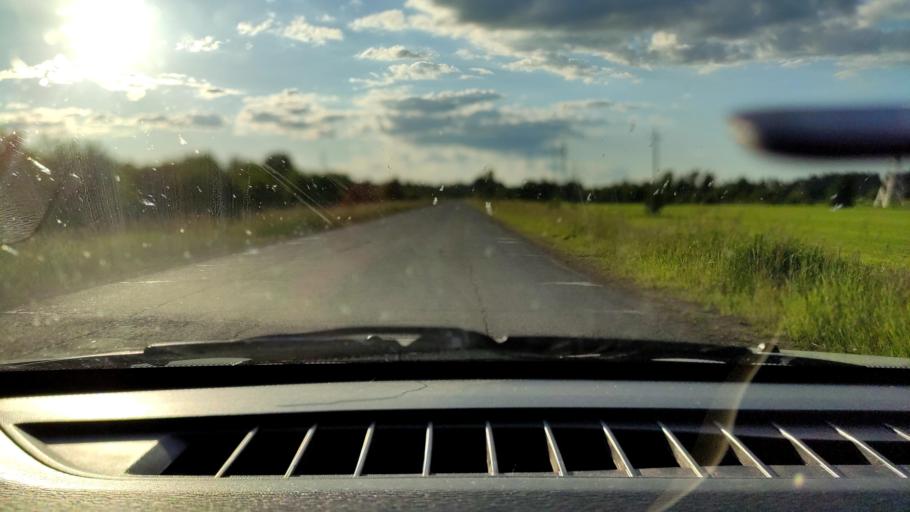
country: RU
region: Perm
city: Uinskoye
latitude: 57.1021
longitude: 56.5393
